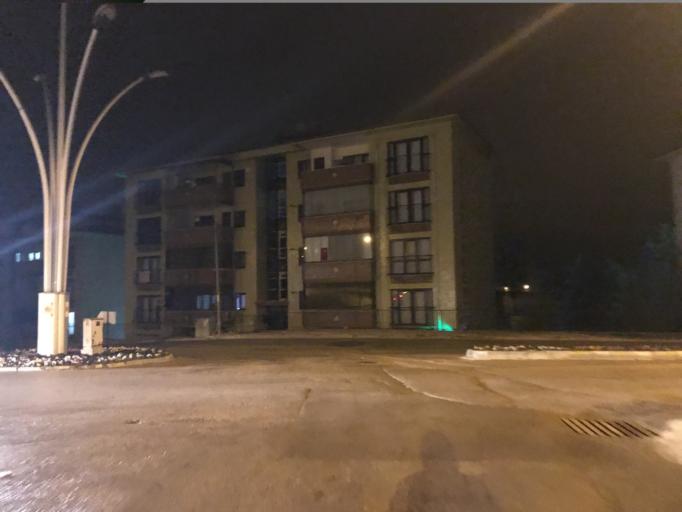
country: TR
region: Karabuk
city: Safranbolu
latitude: 41.2581
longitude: 32.6804
